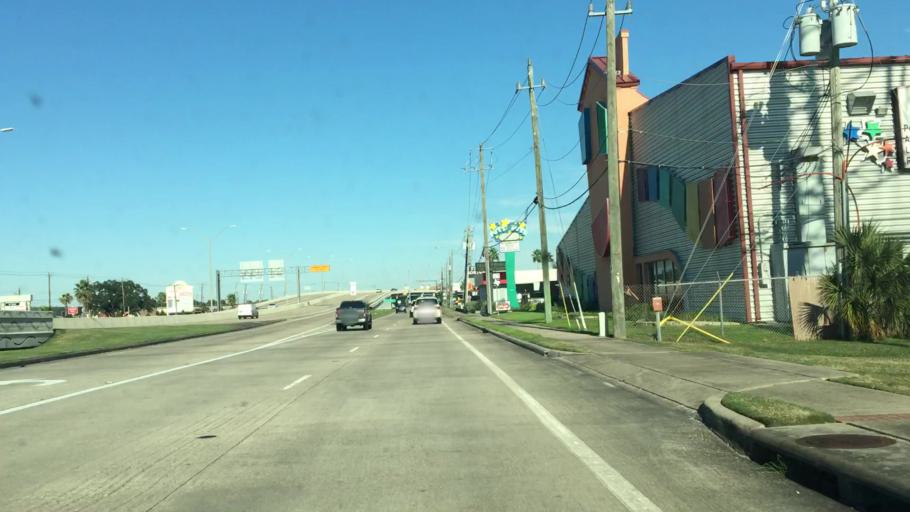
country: US
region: Texas
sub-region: Harris County
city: Webster
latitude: 29.5433
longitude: -95.1096
